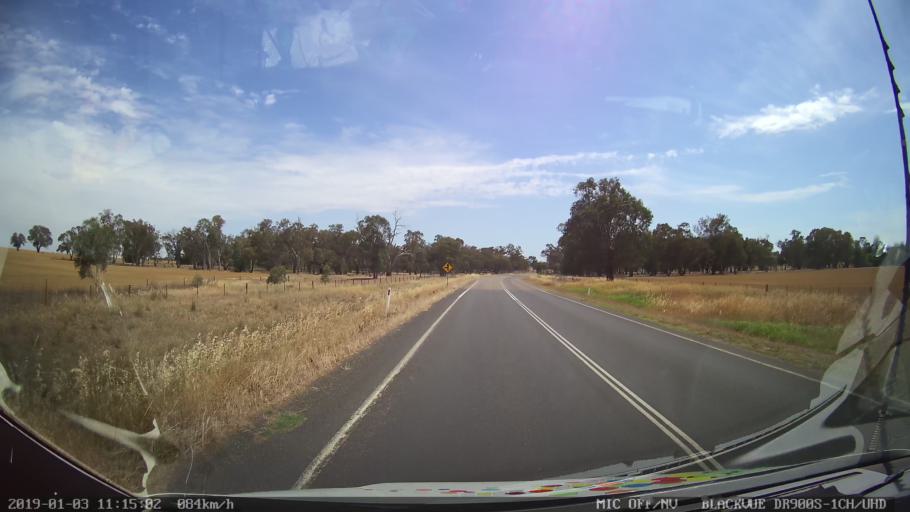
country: AU
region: New South Wales
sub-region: Young
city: Young
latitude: -34.1685
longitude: 148.2619
